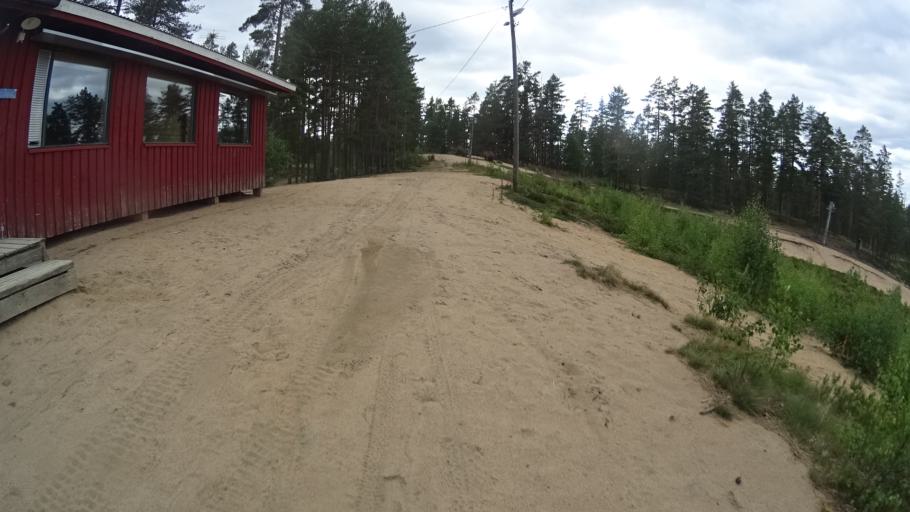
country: FI
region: Satakunta
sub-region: Pohjois-Satakunta
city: Jaemijaervi
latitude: 61.7714
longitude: 22.7498
